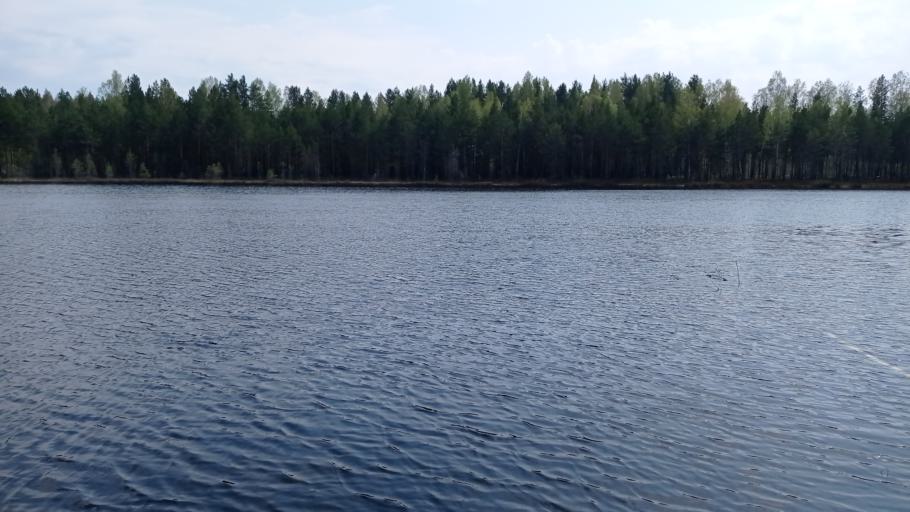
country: RU
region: Tomsk
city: Timiryazevskoye
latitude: 56.4191
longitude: 84.6239
